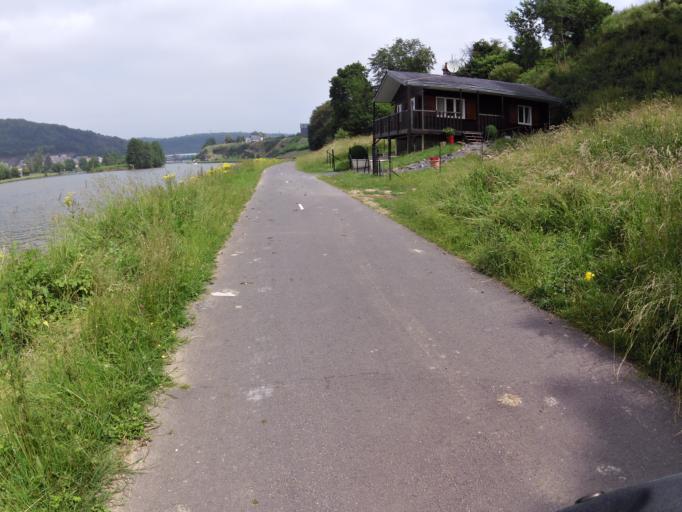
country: FR
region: Champagne-Ardenne
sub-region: Departement des Ardennes
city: Vireux-Molhain
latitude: 50.0776
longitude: 4.7285
